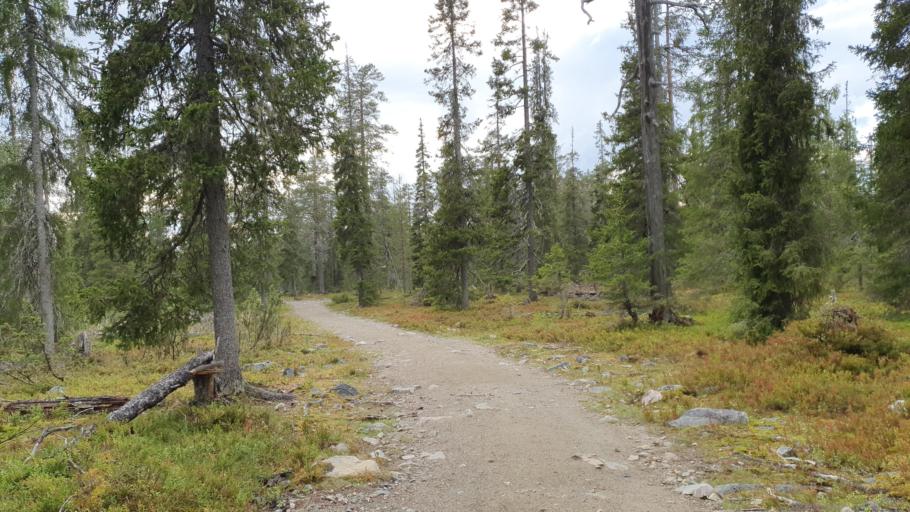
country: FI
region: Lapland
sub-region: Tunturi-Lappi
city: Kolari
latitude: 67.6180
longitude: 24.2453
